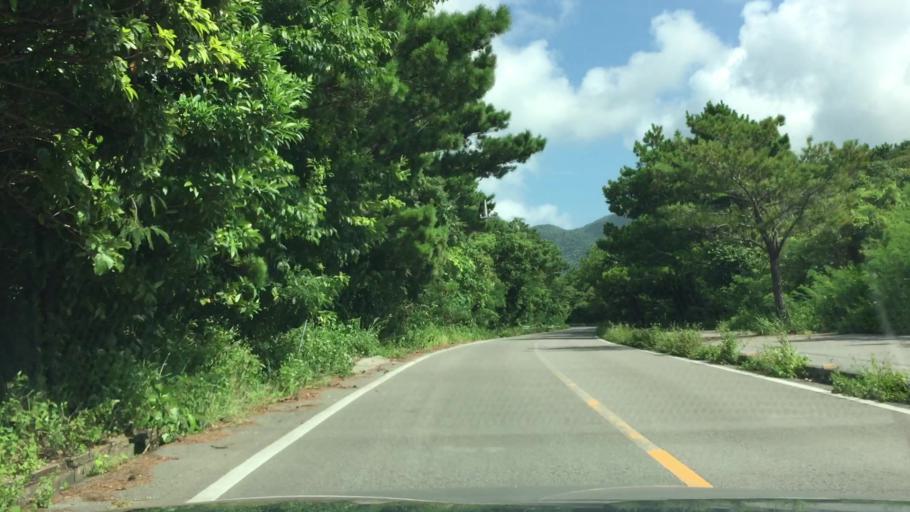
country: JP
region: Okinawa
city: Ishigaki
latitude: 24.4209
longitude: 124.2141
